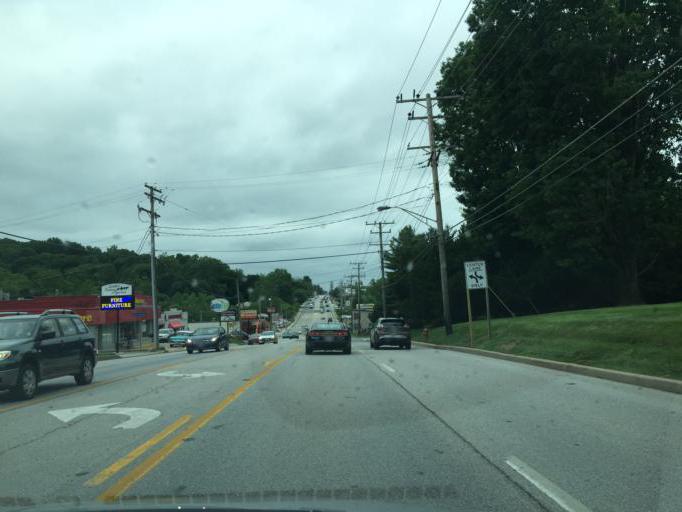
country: US
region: Maryland
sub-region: Baltimore County
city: Cockeysville
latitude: 39.4882
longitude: -76.6470
